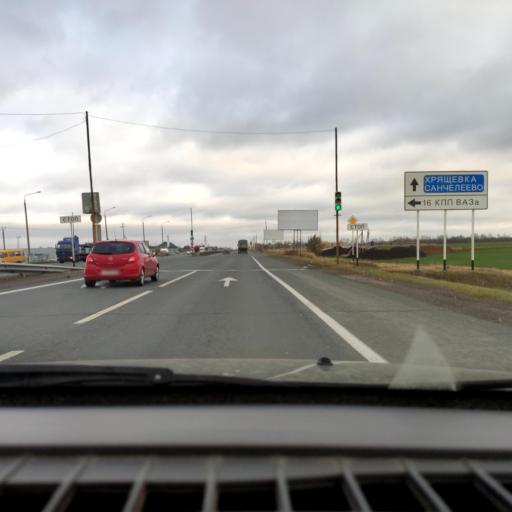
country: RU
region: Samara
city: Tol'yatti
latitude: 53.5560
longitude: 49.3472
